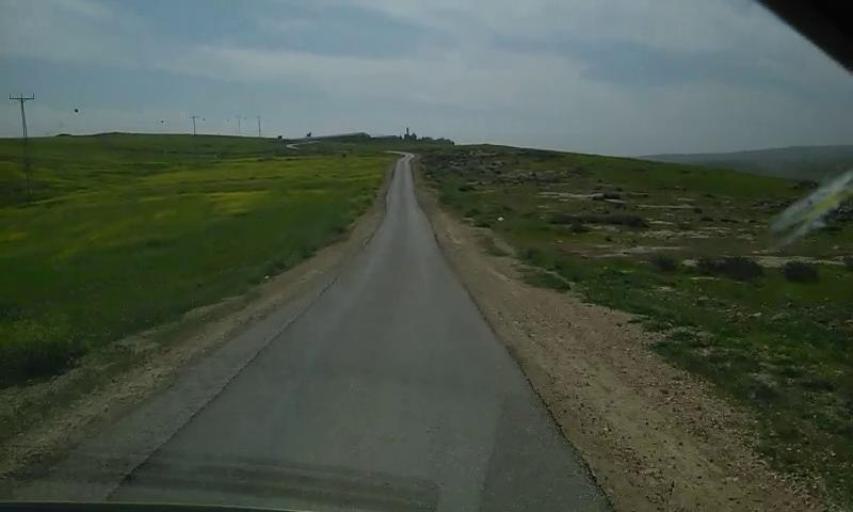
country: PS
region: West Bank
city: Khallat al Mayyah
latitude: 31.4396
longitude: 35.1921
